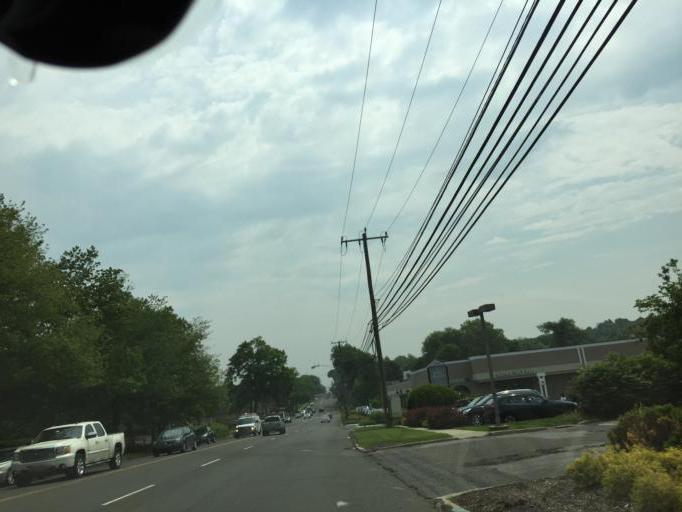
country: US
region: Connecticut
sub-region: Fairfield County
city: Westport
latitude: 41.1389
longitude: -73.3277
